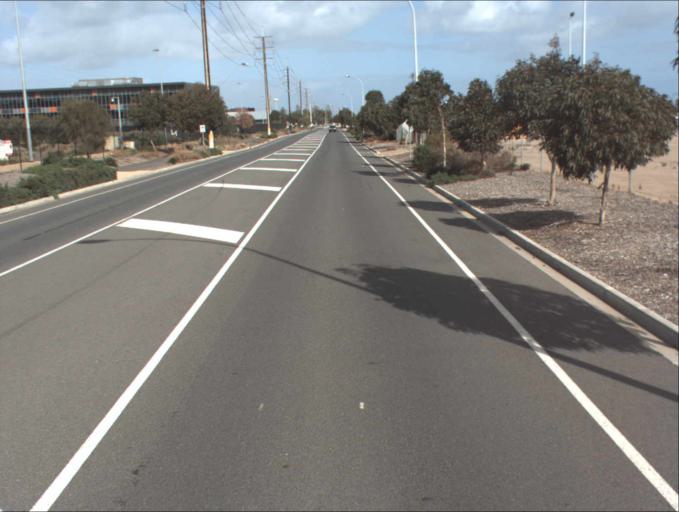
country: AU
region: South Australia
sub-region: Port Adelaide Enfield
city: Birkenhead
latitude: -34.7855
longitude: 138.5071
